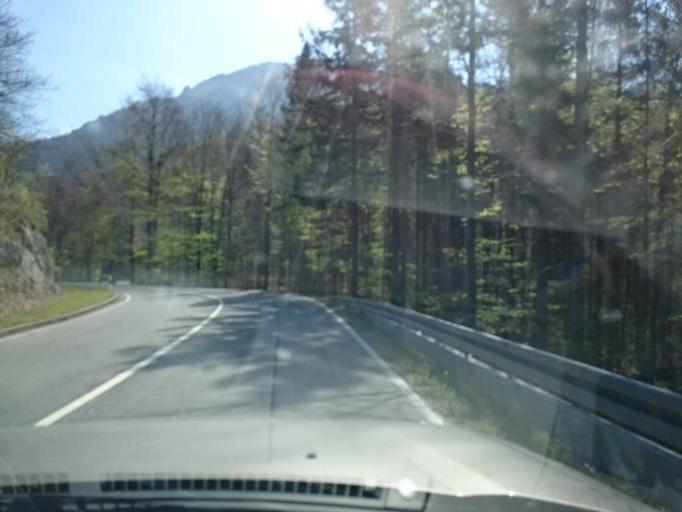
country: DE
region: Bavaria
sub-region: Upper Bavaria
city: Kochel
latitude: 47.6341
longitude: 11.3522
